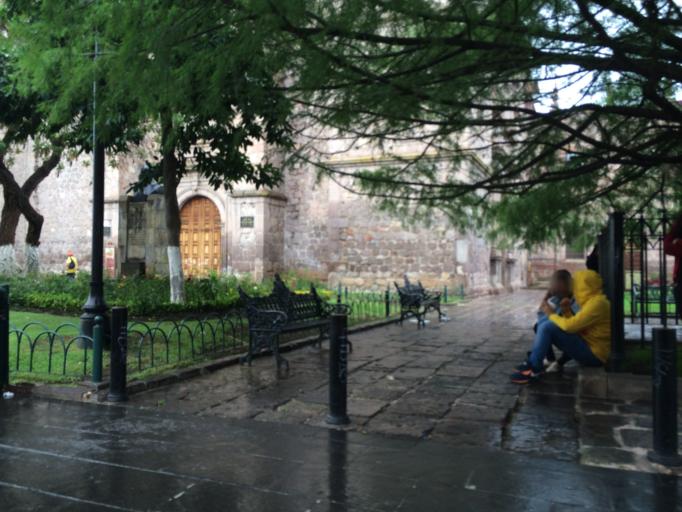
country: MX
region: Michoacan
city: Morelia
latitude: 19.7031
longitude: -101.1952
